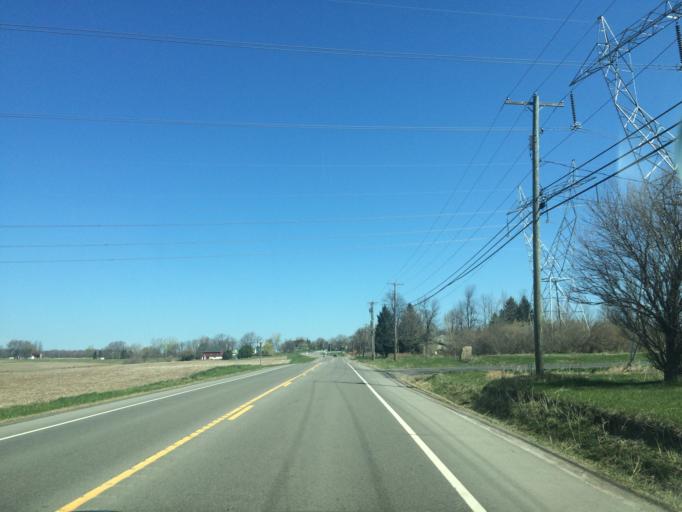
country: US
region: New York
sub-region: Wayne County
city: Macedon
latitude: 43.0880
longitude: -77.3017
